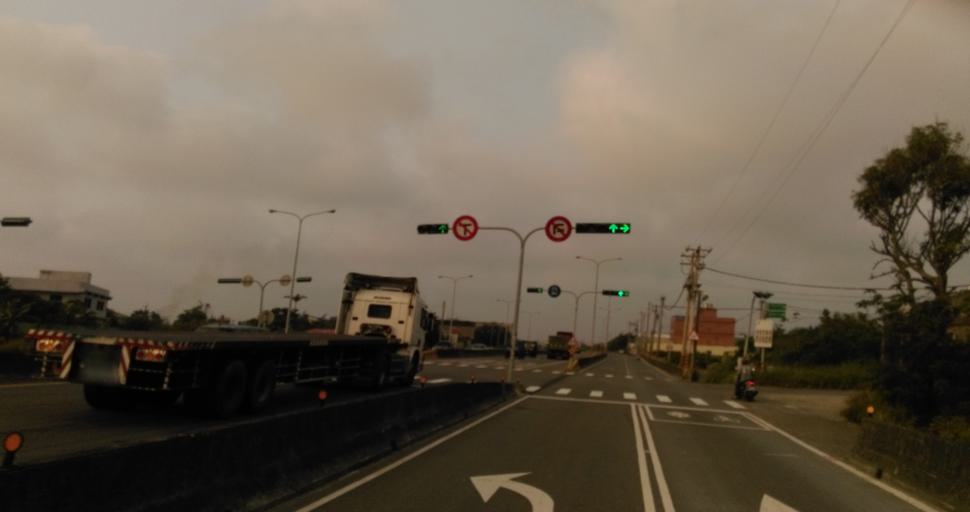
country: TW
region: Taiwan
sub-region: Hsinchu
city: Hsinchu
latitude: 24.7852
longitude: 120.9165
